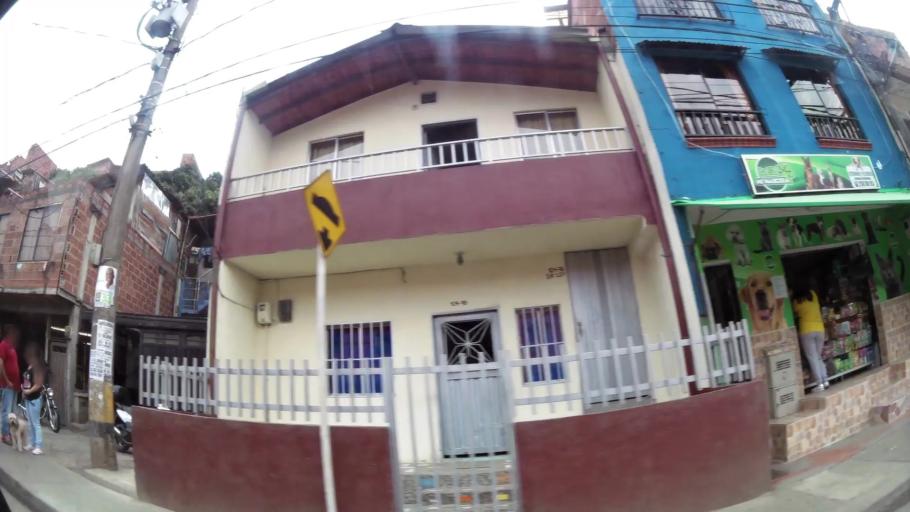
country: CO
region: Antioquia
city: Bello
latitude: 6.2963
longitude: -75.5585
